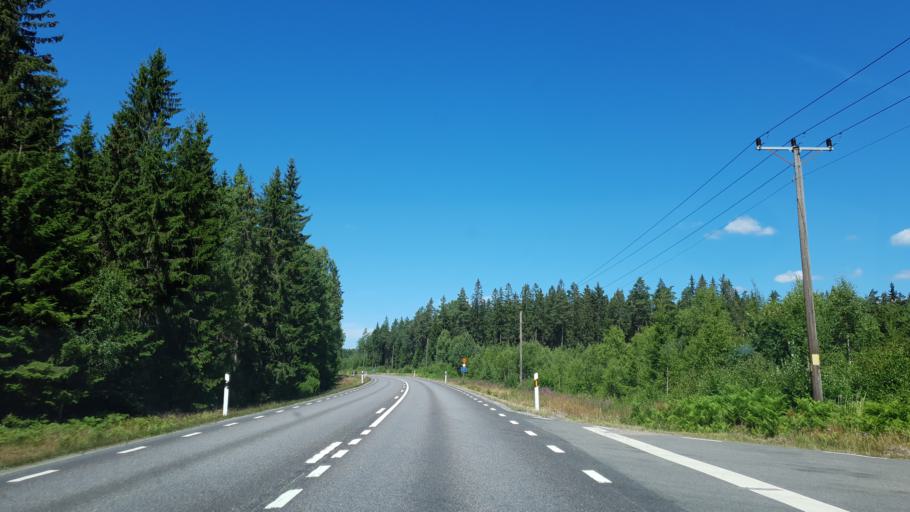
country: SE
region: Joenkoeping
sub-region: Varnamo Kommun
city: Bor
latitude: 57.0508
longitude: 14.2223
